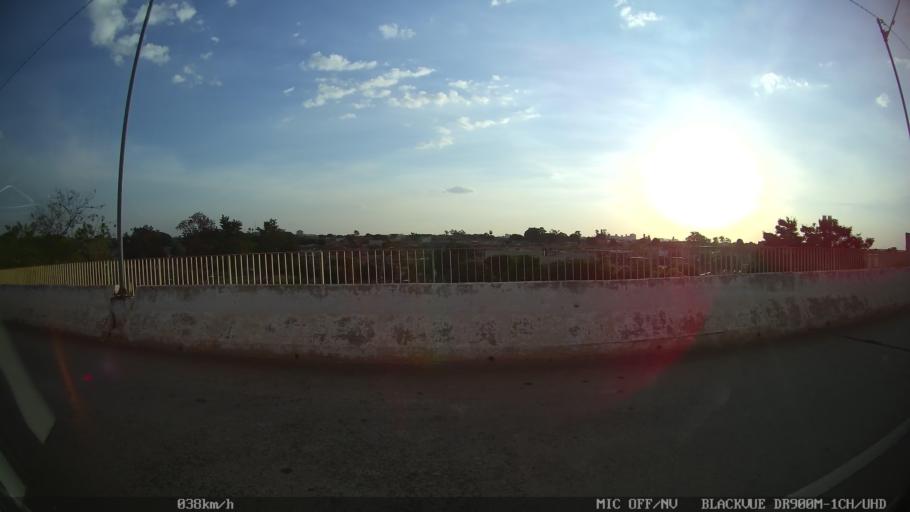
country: BR
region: Sao Paulo
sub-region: Ribeirao Preto
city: Ribeirao Preto
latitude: -21.1373
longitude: -47.8043
